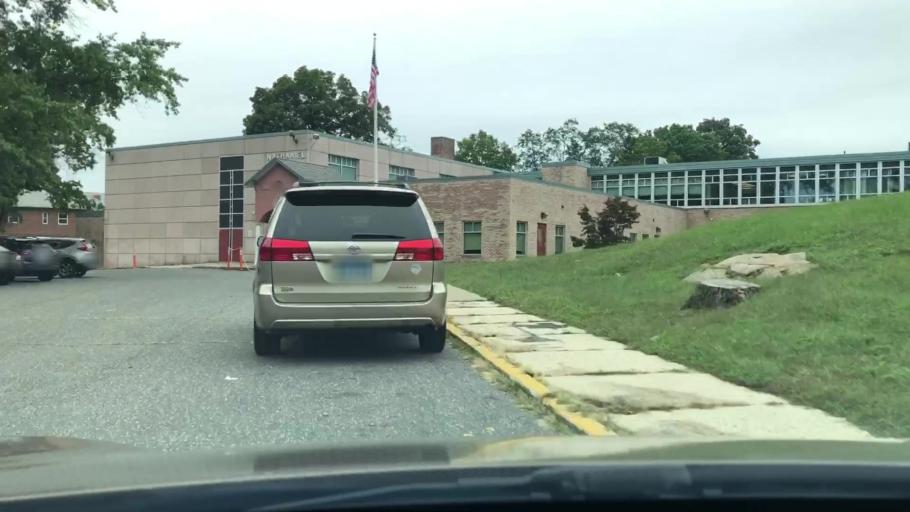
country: US
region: Connecticut
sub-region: Fairfield County
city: East Norwalk
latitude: 41.0815
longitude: -73.4268
